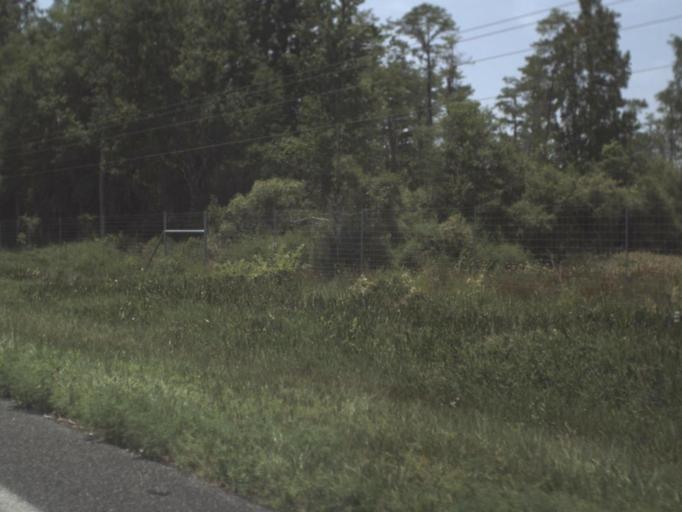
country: US
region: Florida
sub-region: Taylor County
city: Steinhatchee
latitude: 29.8322
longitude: -83.3631
